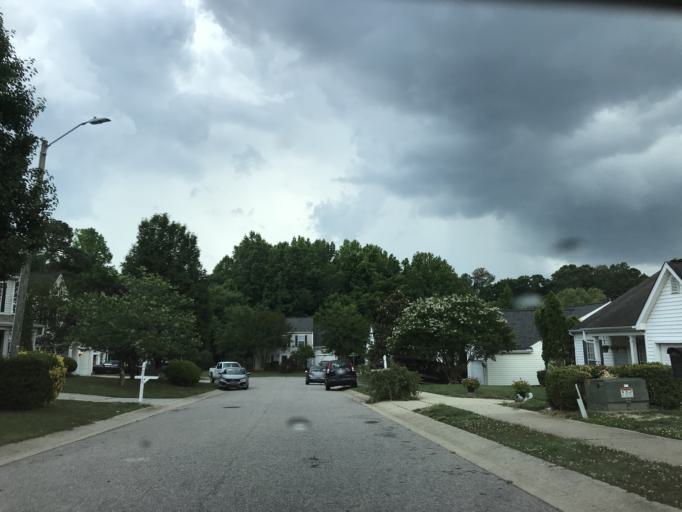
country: US
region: North Carolina
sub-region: Wake County
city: Knightdale
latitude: 35.8518
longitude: -78.5507
